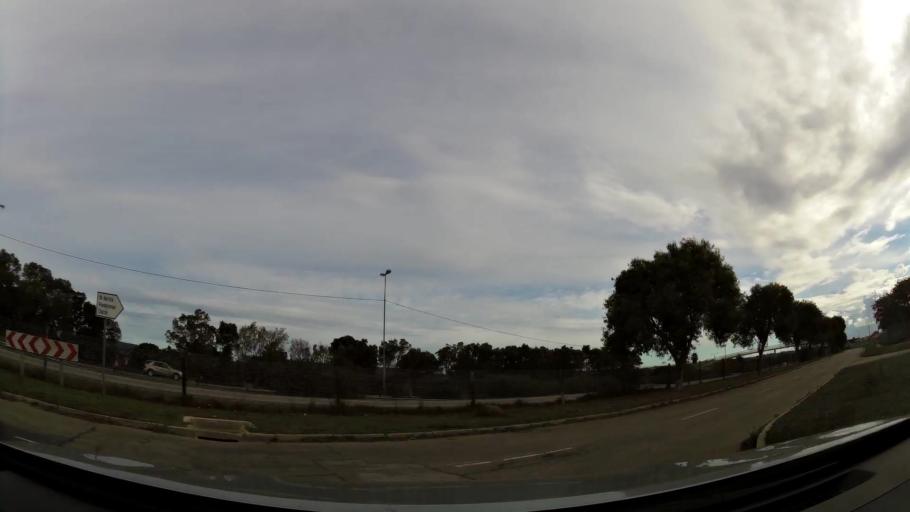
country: ZA
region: Eastern Cape
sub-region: Nelson Mandela Bay Metropolitan Municipality
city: Port Elizabeth
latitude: -33.9450
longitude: 25.4941
